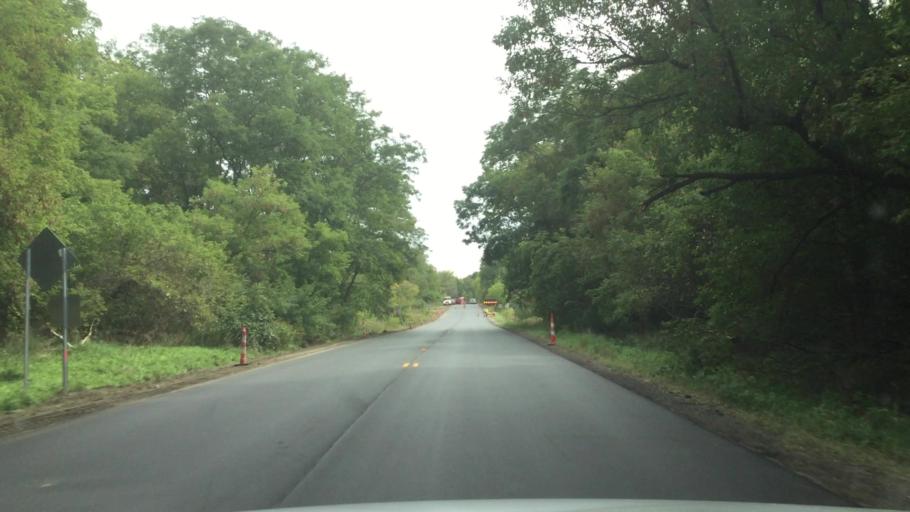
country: US
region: Michigan
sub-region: Oakland County
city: Holly
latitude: 42.8139
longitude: -83.6025
